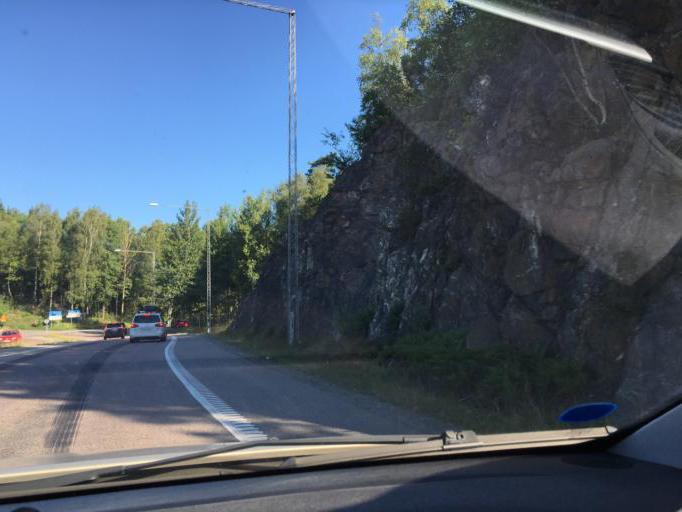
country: SE
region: Stockholm
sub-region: Salems Kommun
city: Ronninge
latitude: 59.2128
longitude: 17.7581
